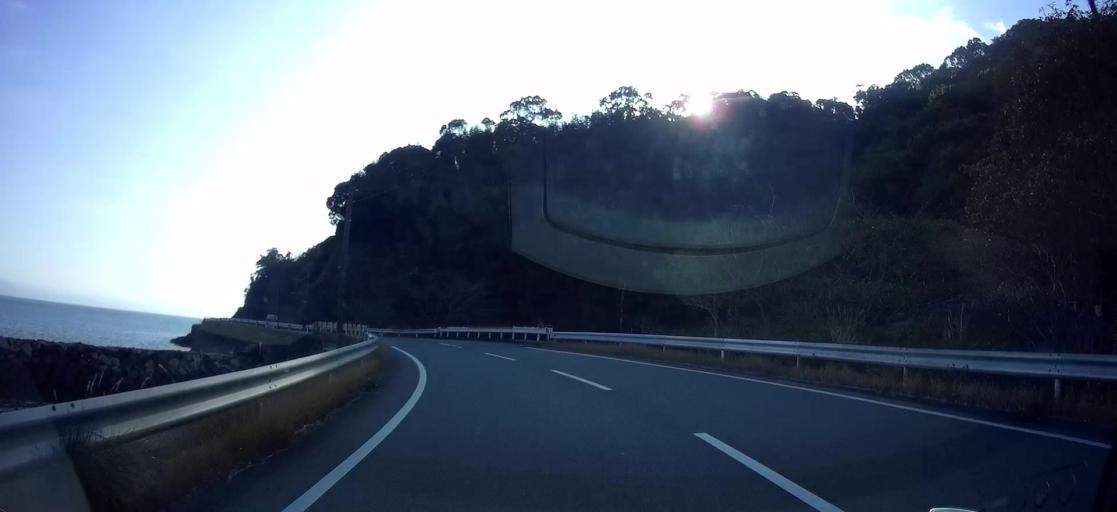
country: JP
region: Kumamoto
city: Minamata
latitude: 32.3871
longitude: 130.3819
